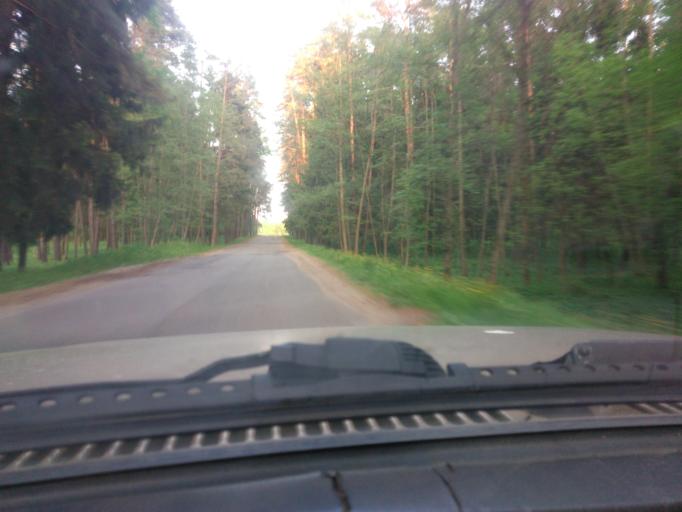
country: BY
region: Mogilev
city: Mahilyow
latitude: 53.9308
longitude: 30.3025
